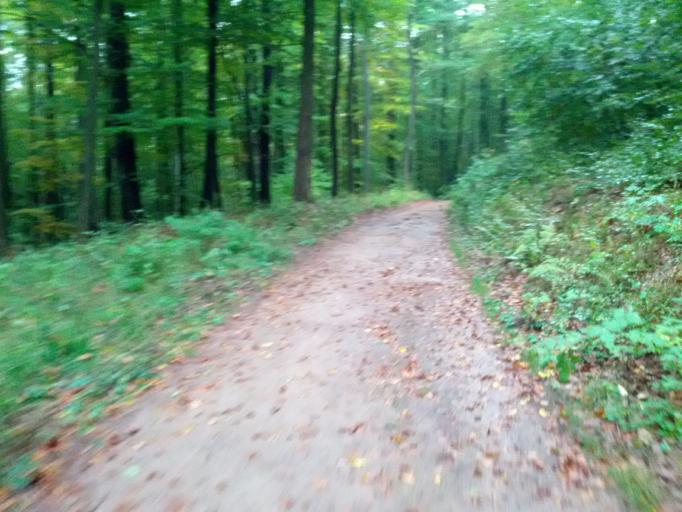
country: DE
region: Thuringia
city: Eisenach
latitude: 50.9567
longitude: 10.3386
